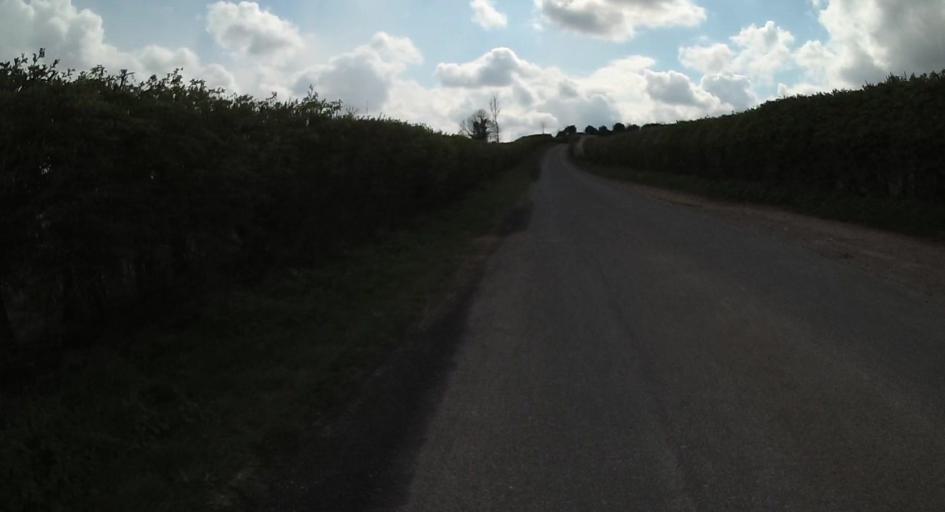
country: GB
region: England
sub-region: Hampshire
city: Kings Worthy
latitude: 51.1037
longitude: -1.2006
